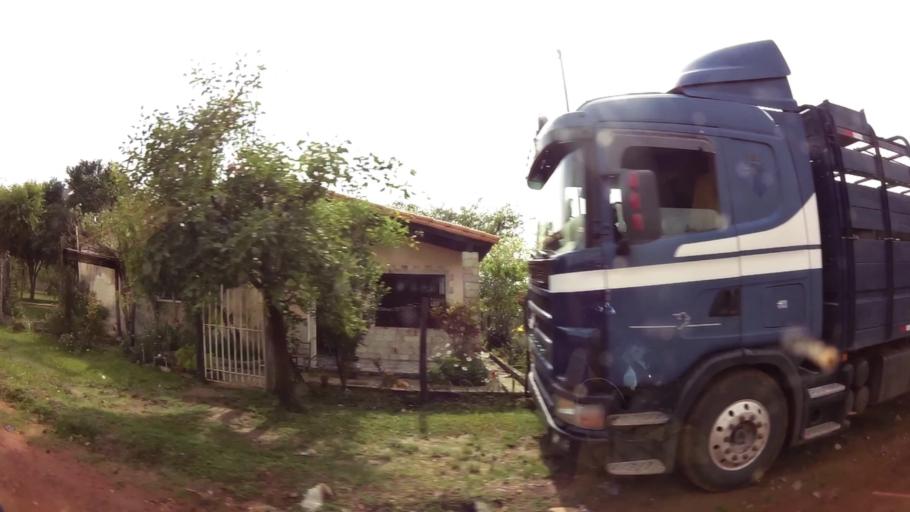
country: PY
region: Presidente Hayes
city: Villa Hayes
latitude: -25.1171
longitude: -57.4830
